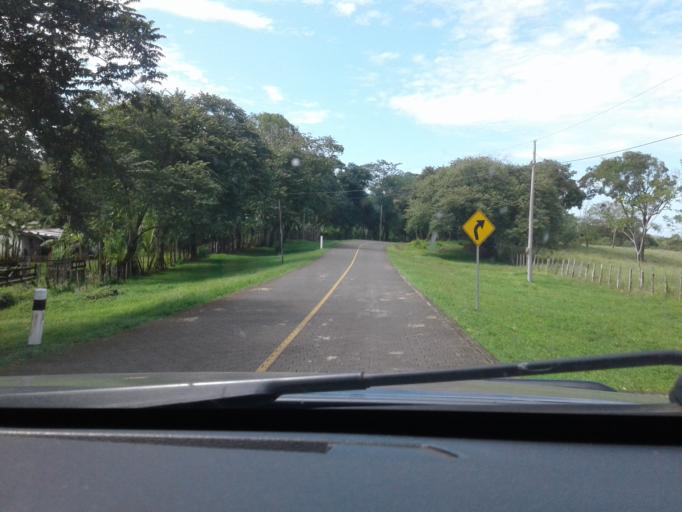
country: NI
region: Rivas
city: Cardenas
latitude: 11.1719
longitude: -85.4788
